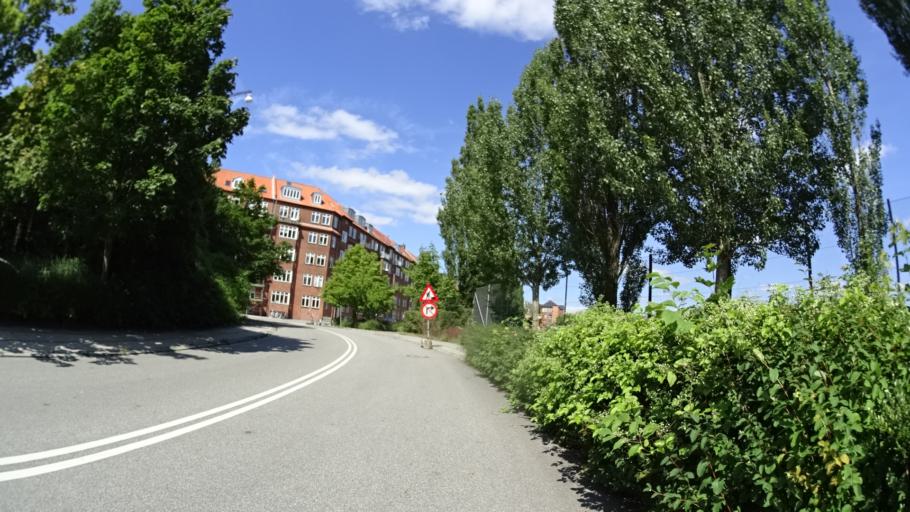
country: DK
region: Central Jutland
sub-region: Arhus Kommune
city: Arhus
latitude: 56.1413
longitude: 10.1961
